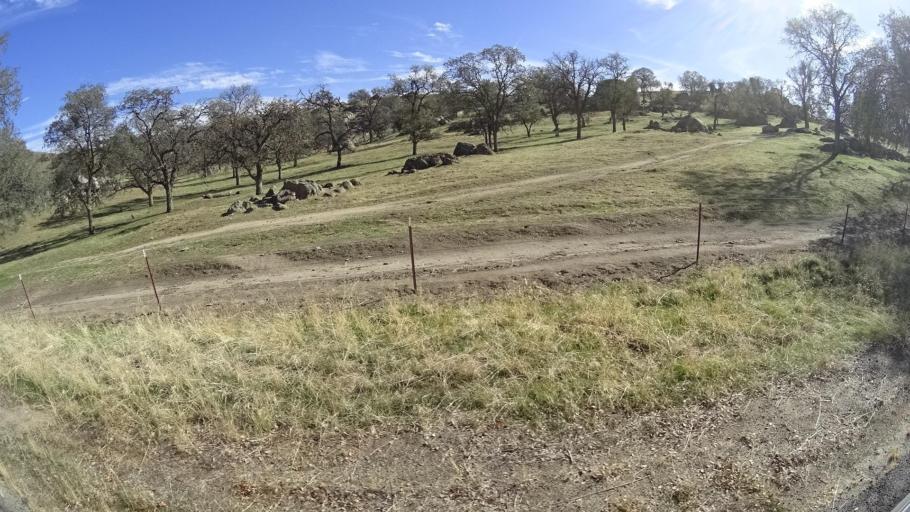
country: US
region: California
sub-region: Kern County
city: Oildale
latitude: 35.6277
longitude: -118.8448
